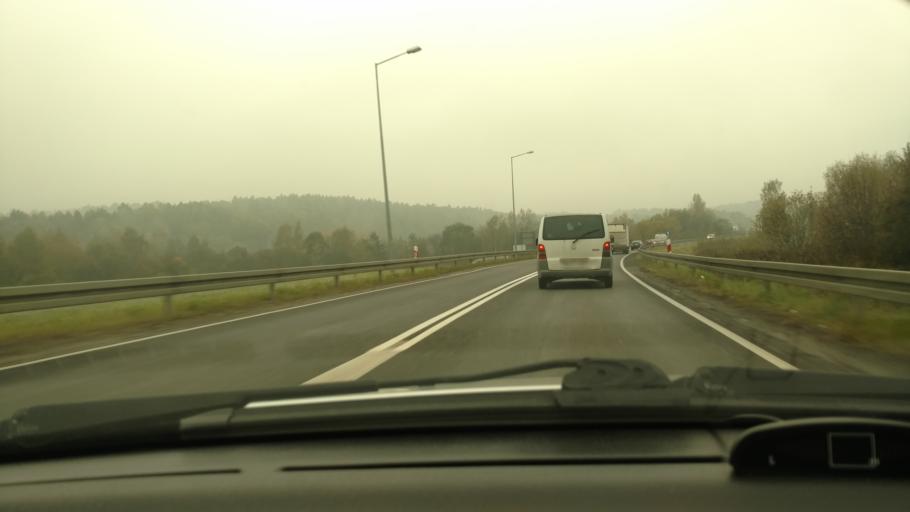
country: PL
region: Lesser Poland Voivodeship
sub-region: Powiat gorlicki
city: Kobylanka
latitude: 49.6759
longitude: 21.1905
